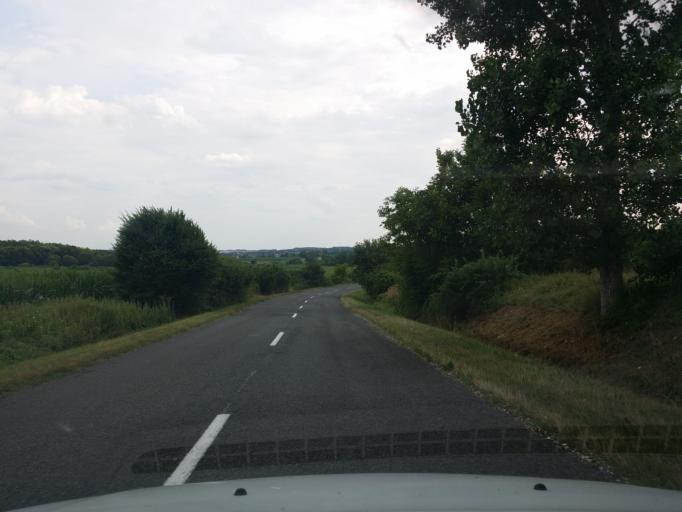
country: HU
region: Nograd
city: Bercel
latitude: 47.9004
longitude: 19.3715
